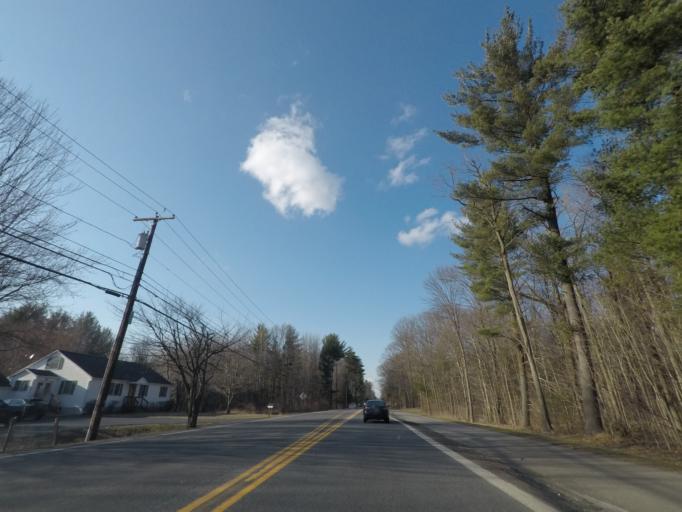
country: US
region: New York
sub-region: Saratoga County
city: Country Knolls
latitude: 42.8409
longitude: -73.7940
